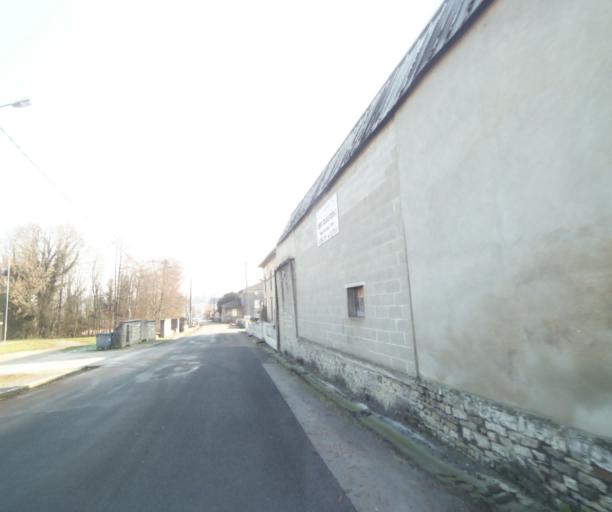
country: FR
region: Champagne-Ardenne
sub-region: Departement de la Haute-Marne
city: Wassy
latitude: 48.4723
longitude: 4.9663
